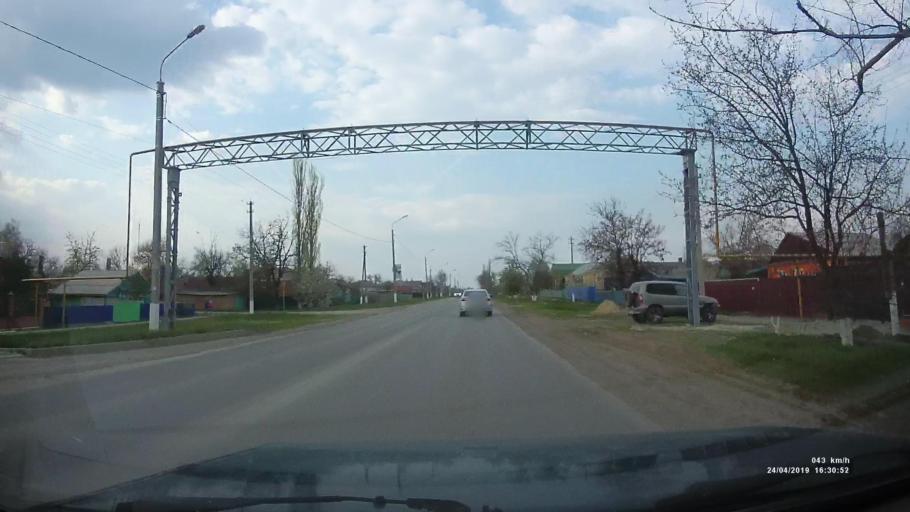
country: RU
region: Rostov
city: Orlovskiy
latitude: 46.8770
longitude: 42.0384
